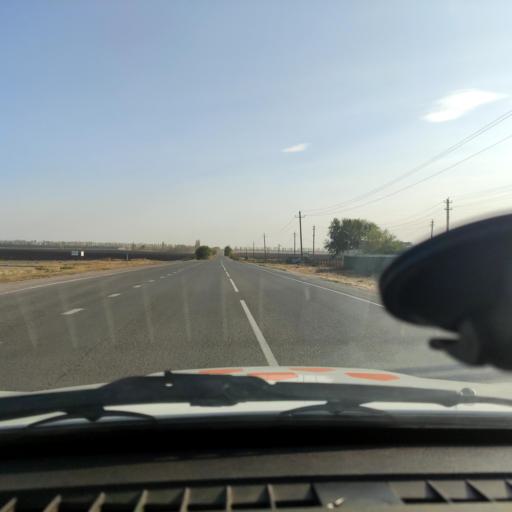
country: RU
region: Voronezj
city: Novaya Usman'
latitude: 51.5817
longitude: 39.3747
